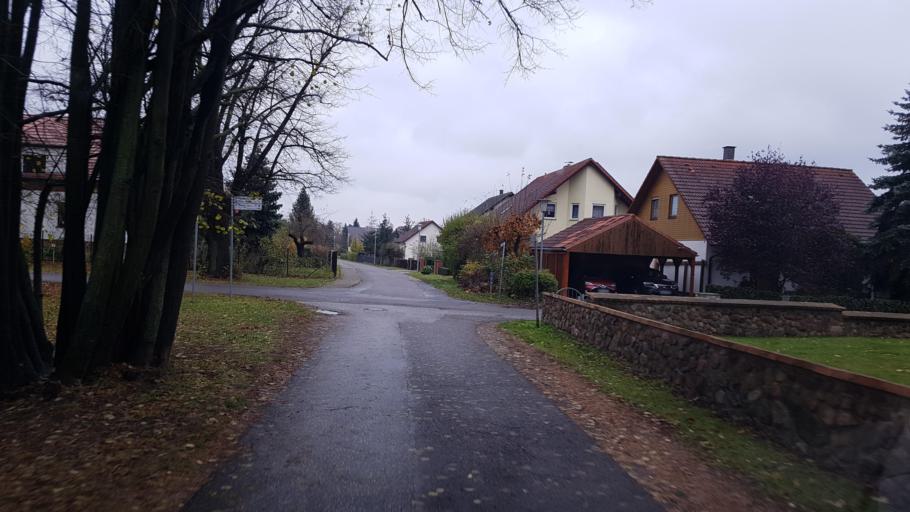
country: DE
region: Brandenburg
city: Drebkau
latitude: 51.6973
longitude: 14.2472
